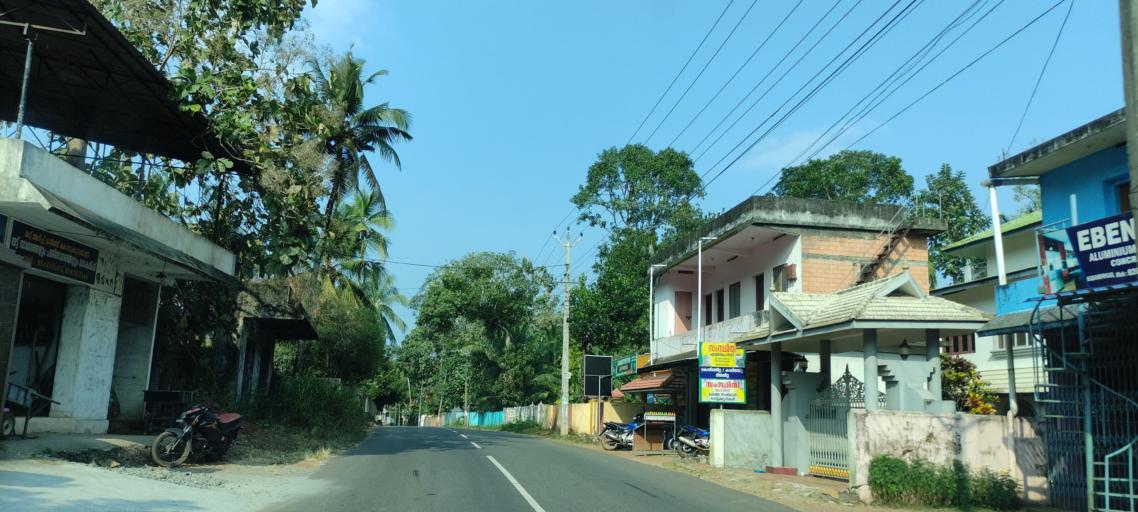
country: IN
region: Kerala
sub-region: Pattanamtitta
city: Adur
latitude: 9.0865
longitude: 76.6822
